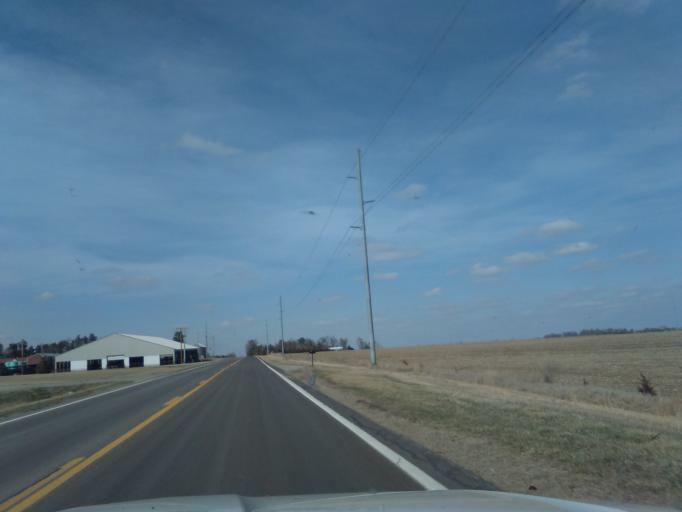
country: US
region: Nebraska
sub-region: Gage County
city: Beatrice
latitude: 40.1974
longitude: -96.9353
